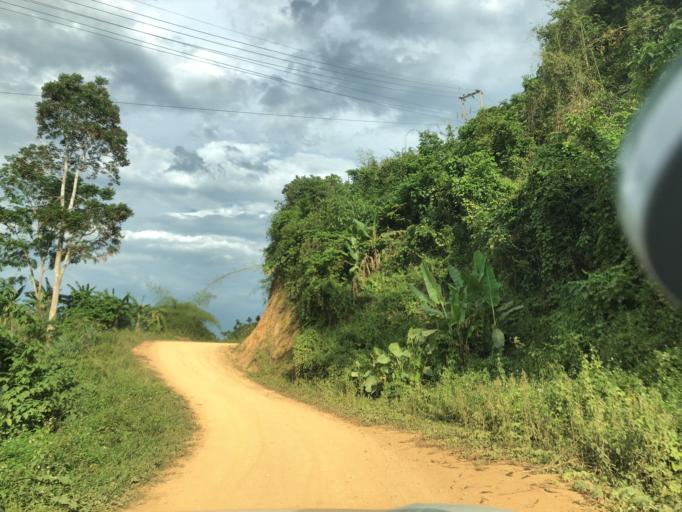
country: TH
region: Loei
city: Chiang Khan
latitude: 18.0265
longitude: 101.4171
